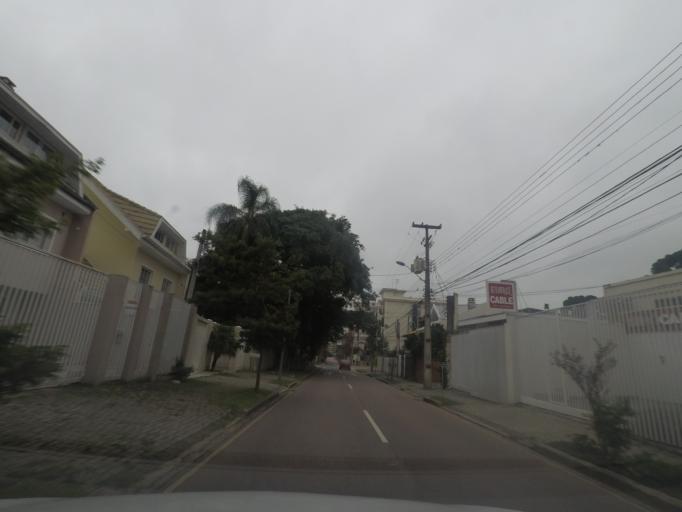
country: BR
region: Parana
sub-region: Curitiba
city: Curitiba
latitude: -25.4217
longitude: -49.2581
